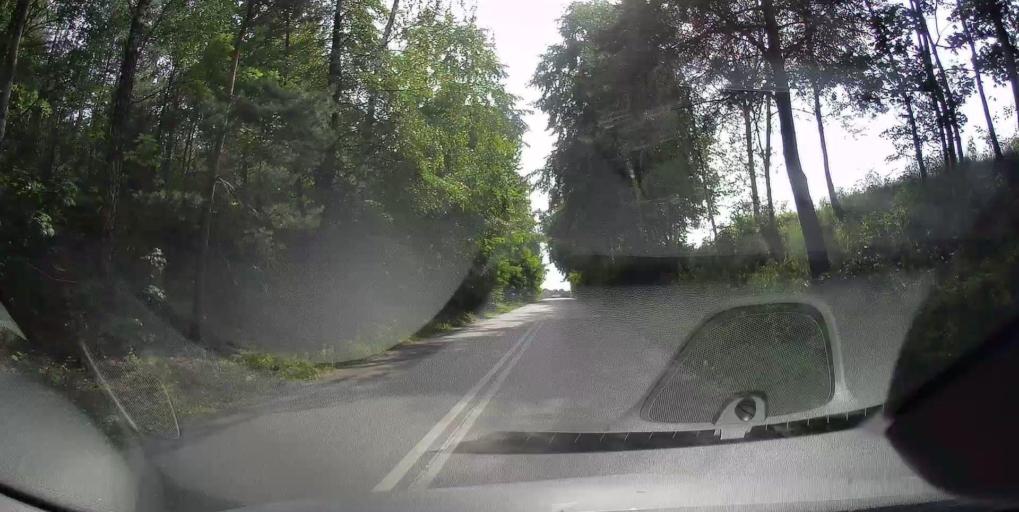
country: PL
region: Lodz Voivodeship
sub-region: Powiat tomaszowski
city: Tomaszow Mazowiecki
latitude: 51.4938
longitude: 19.9918
